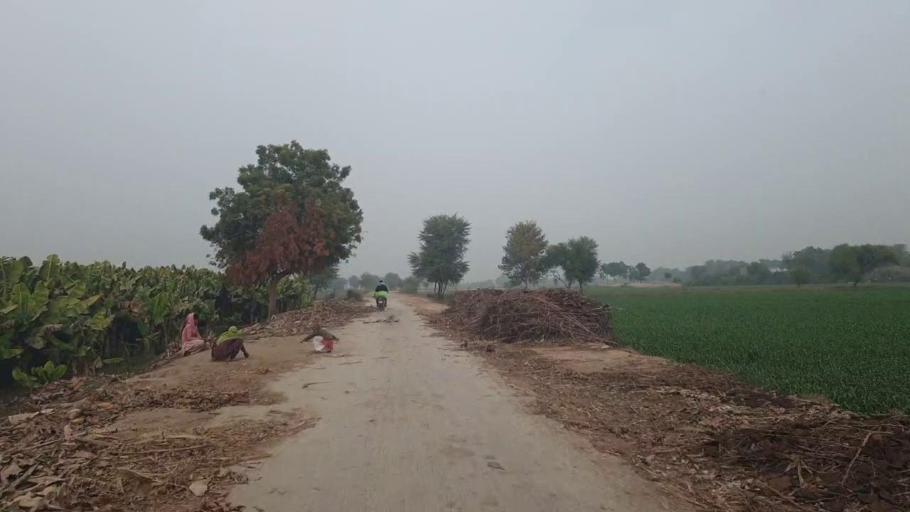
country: PK
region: Sindh
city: Tando Adam
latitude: 25.7642
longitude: 68.7026
